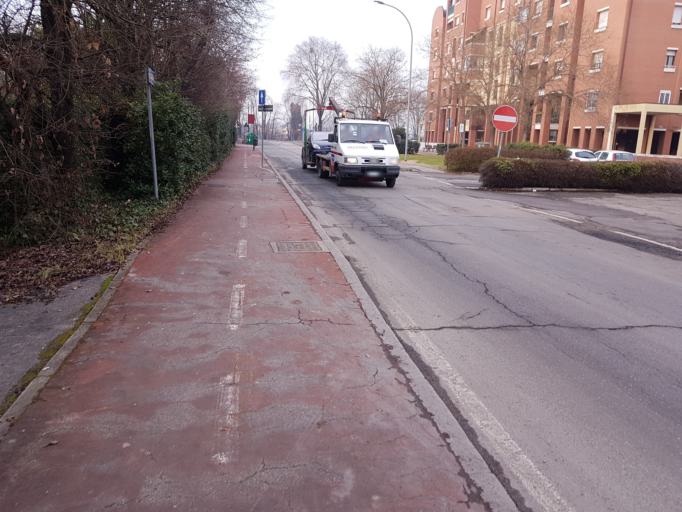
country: IT
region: Emilia-Romagna
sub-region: Provincia di Bologna
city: Quarto Inferiore
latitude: 44.5097
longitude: 11.3839
